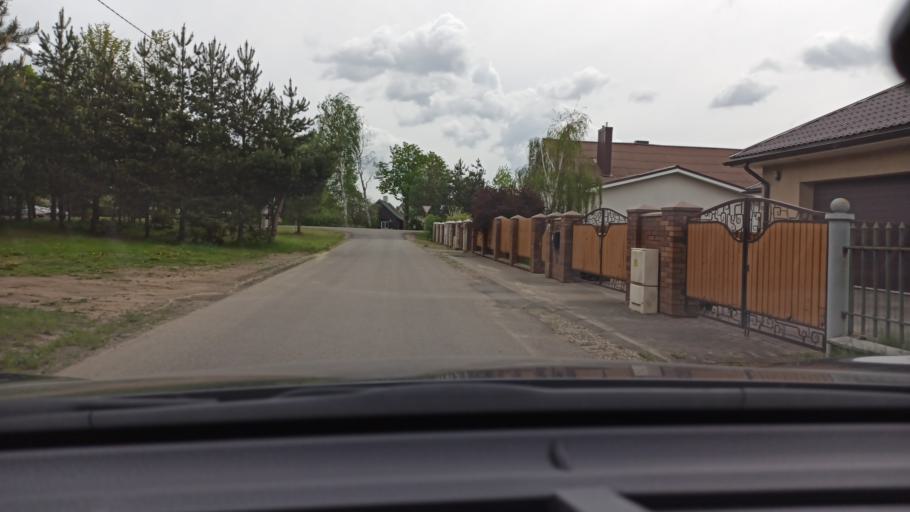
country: LT
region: Siauliu apskritis
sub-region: Siauliai
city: Siauliai
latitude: 55.9034
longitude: 23.3321
